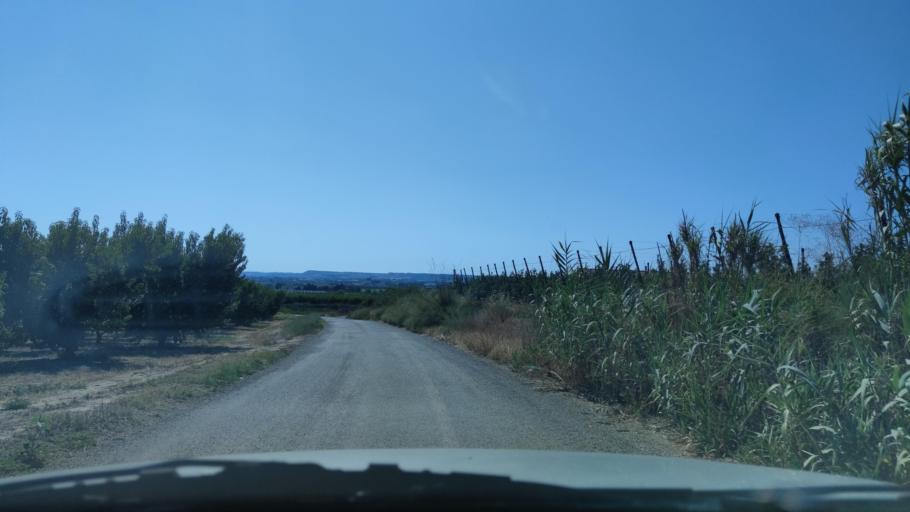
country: ES
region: Catalonia
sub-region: Provincia de Lleida
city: Corbins
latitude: 41.6782
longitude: 0.6686
